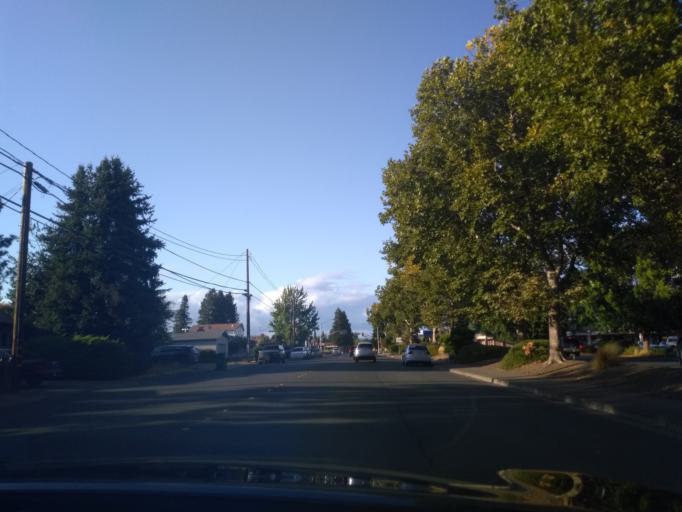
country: US
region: California
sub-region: Mendocino County
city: Ukiah
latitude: 39.1499
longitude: -123.1990
